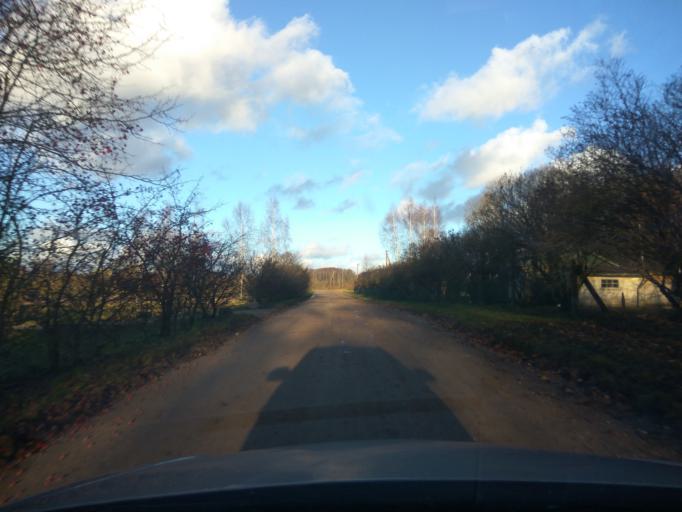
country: LV
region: Aizpute
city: Aizpute
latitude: 56.7541
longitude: 21.7774
